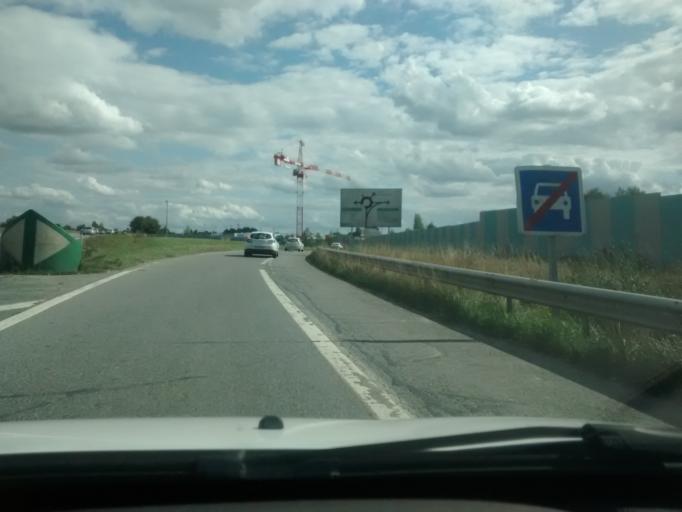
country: FR
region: Brittany
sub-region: Departement d'Ille-et-Vilaine
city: Saint-Jacques-de-la-Lande
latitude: 48.0921
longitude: -1.7076
